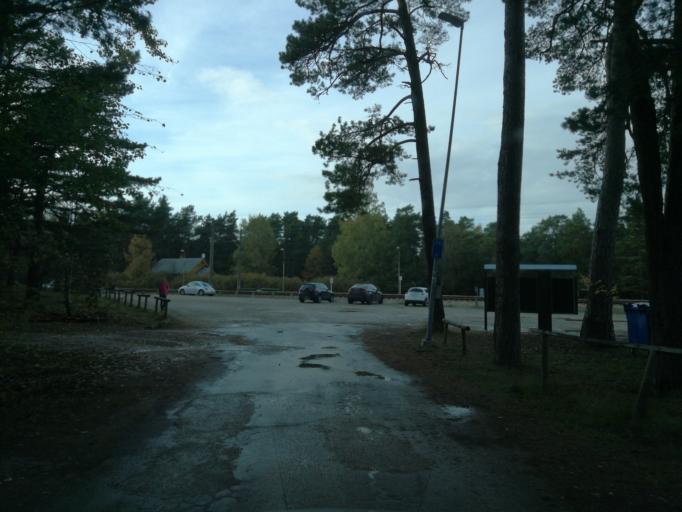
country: LV
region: Riga
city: Jaunciems
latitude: 57.0856
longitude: 24.1535
